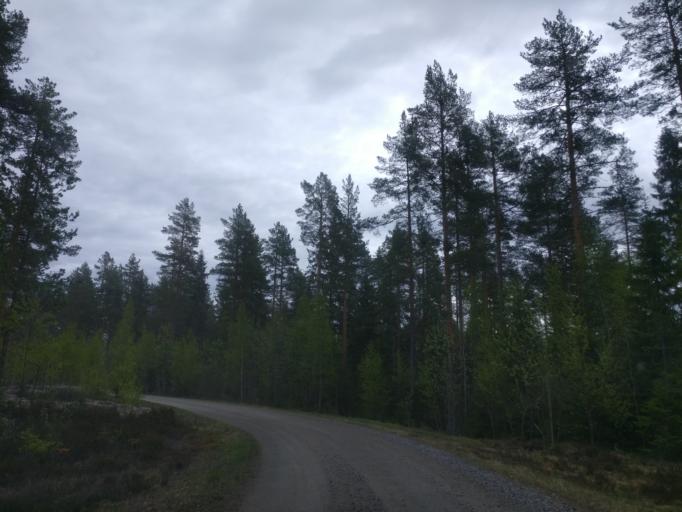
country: SE
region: Gaevleborg
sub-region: Soderhamns Kommun
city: Soderhamn
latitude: 61.4208
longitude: 16.9038
